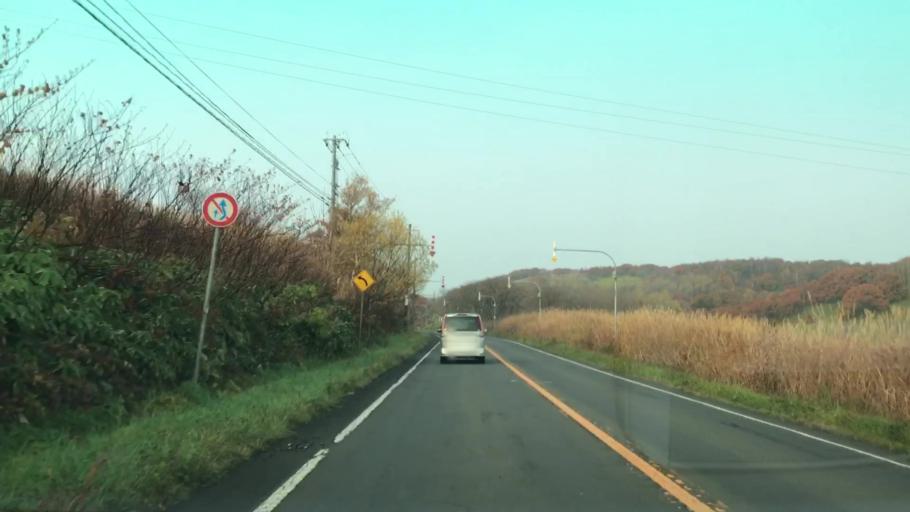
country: JP
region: Hokkaido
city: Ishikari
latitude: 43.3346
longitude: 141.4364
